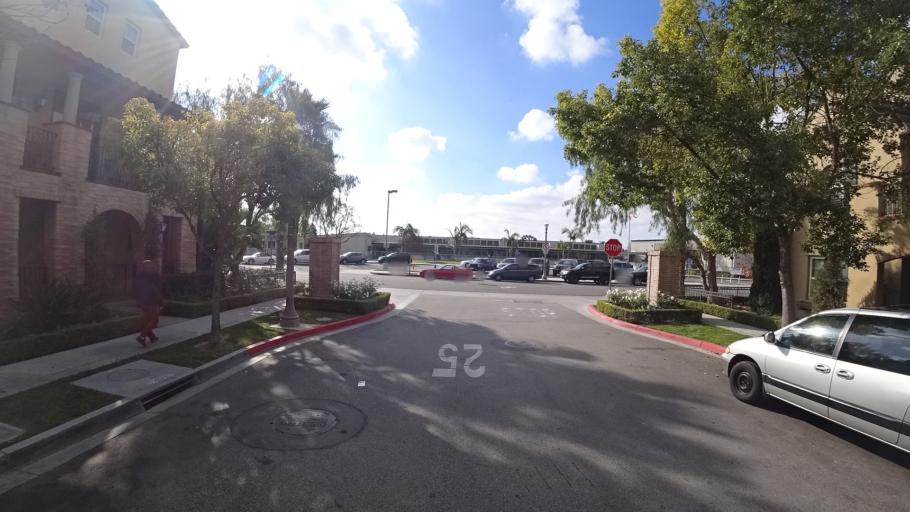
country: US
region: California
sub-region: Orange County
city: Anaheim
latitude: 33.8281
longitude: -117.9062
